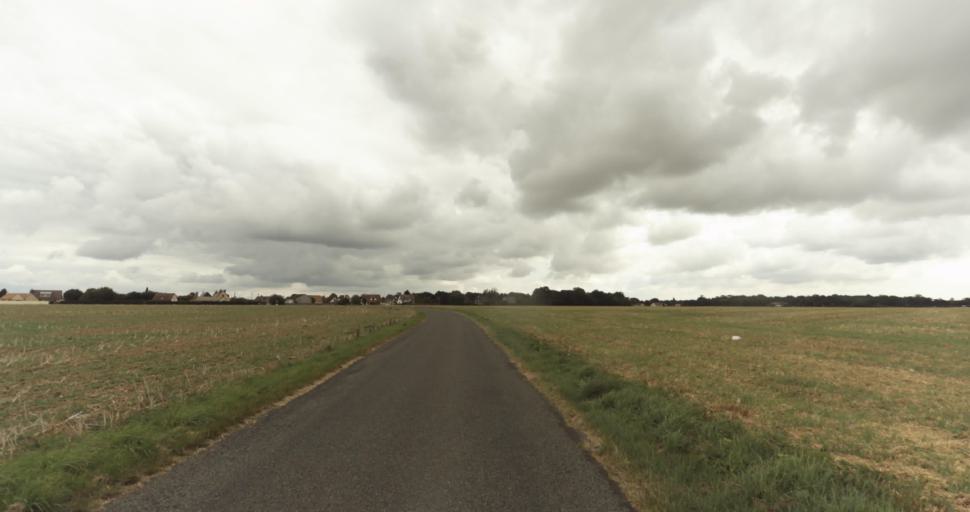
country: FR
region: Haute-Normandie
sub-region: Departement de l'Eure
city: Gravigny
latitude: 49.0149
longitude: 1.2630
